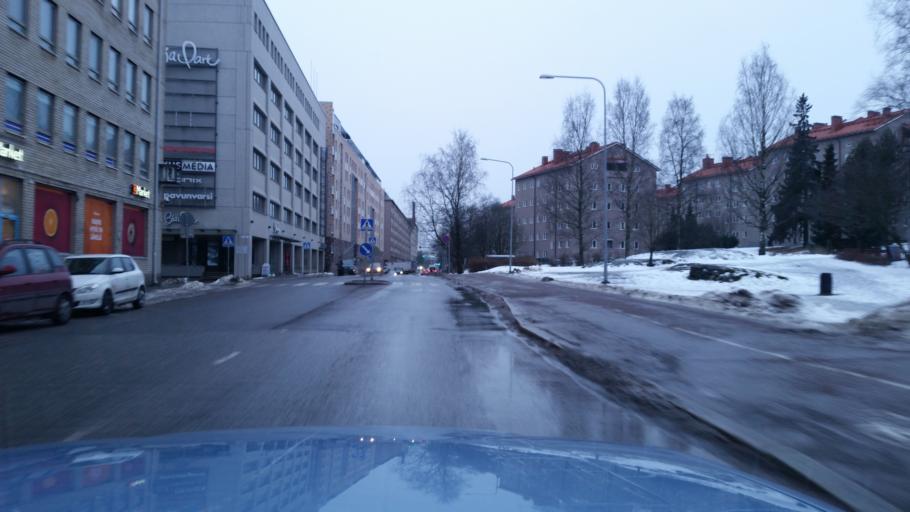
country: FI
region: Uusimaa
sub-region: Helsinki
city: Helsinki
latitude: 60.2124
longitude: 24.9784
